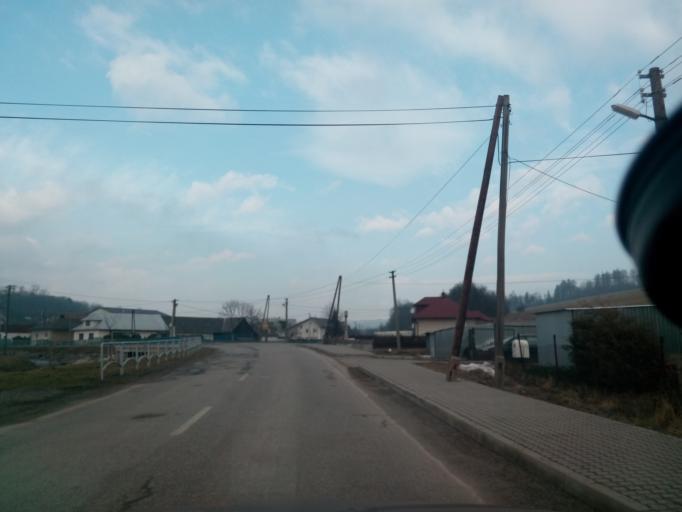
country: SK
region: Presovsky
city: Lipany
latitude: 49.1756
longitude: 20.8686
